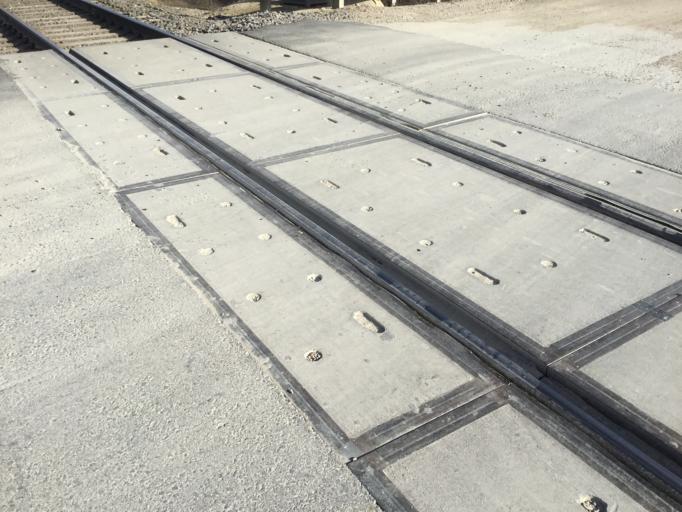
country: US
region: Kansas
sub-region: Chase County
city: Cottonwood Falls
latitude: 38.3761
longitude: -96.4683
